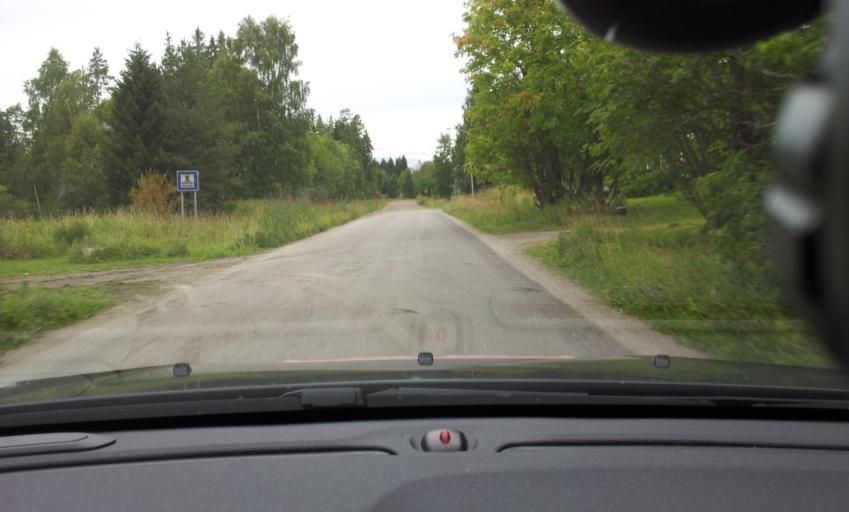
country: SE
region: Jaemtland
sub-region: OEstersunds Kommun
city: Brunflo
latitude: 62.9577
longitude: 15.0326
